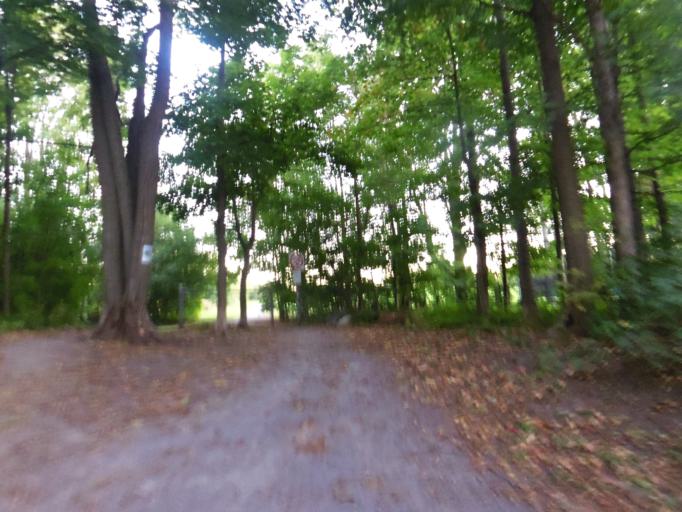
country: CA
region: Ontario
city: Ottawa
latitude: 45.3894
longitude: -75.6547
